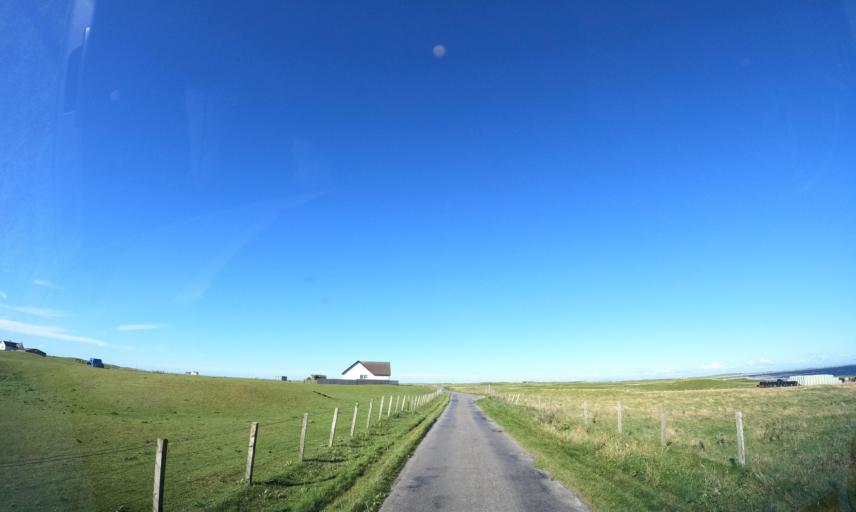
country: GB
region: Scotland
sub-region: Eilean Siar
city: Barra
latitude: 56.4737
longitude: -6.8995
